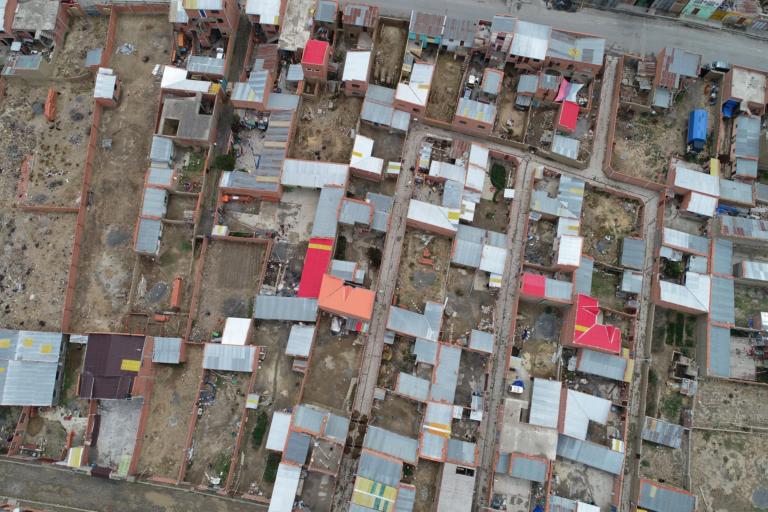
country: BO
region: La Paz
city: Achacachi
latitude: -16.0517
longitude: -68.6806
